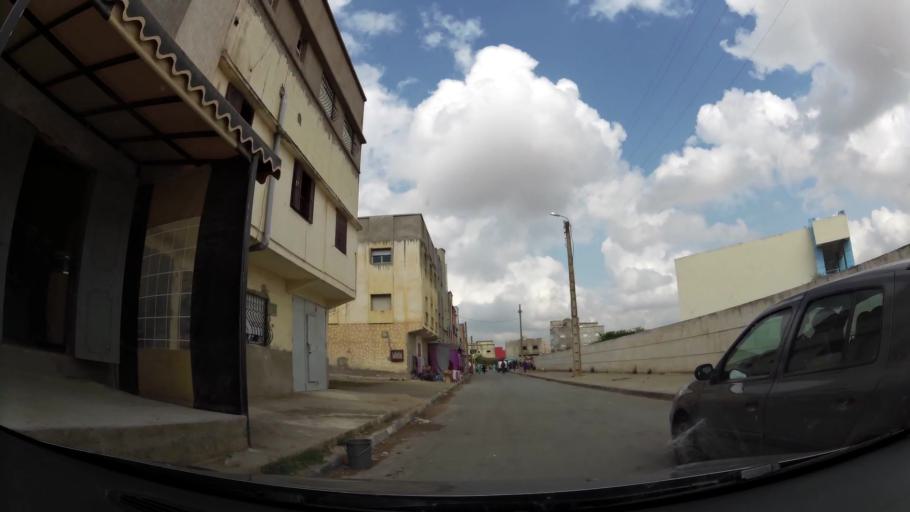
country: MA
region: Rabat-Sale-Zemmour-Zaer
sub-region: Khemisset
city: Tiflet
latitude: 33.8969
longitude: -6.3292
